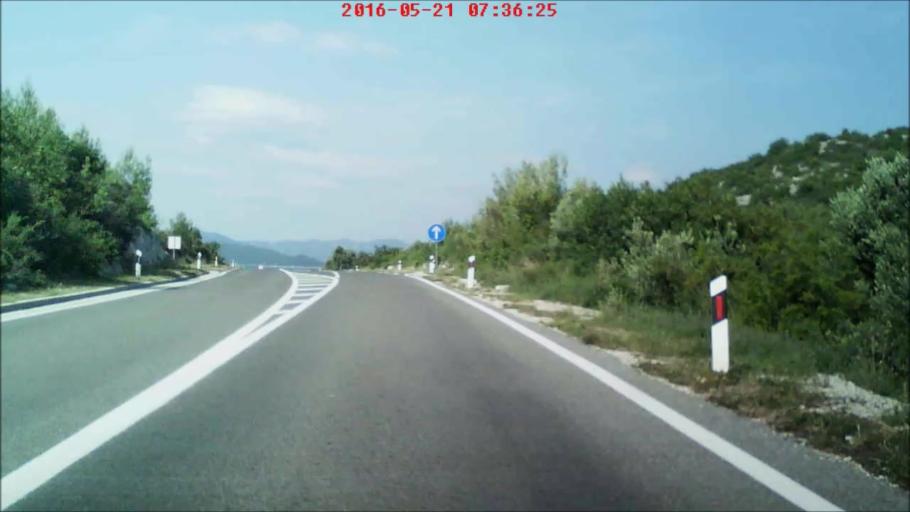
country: HR
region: Dubrovacko-Neretvanska
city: Podgora
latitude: 42.7878
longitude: 17.8656
